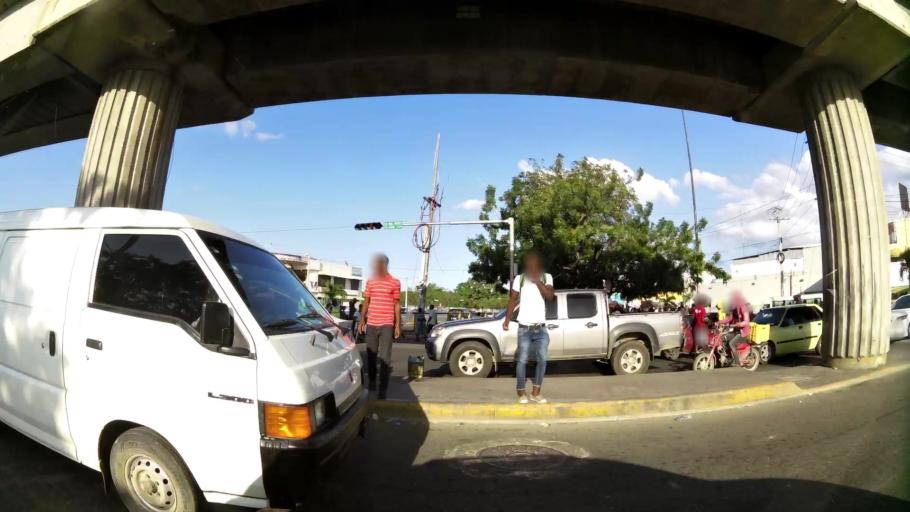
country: DO
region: Nacional
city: Ensanche Luperon
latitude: 18.5453
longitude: -69.9004
